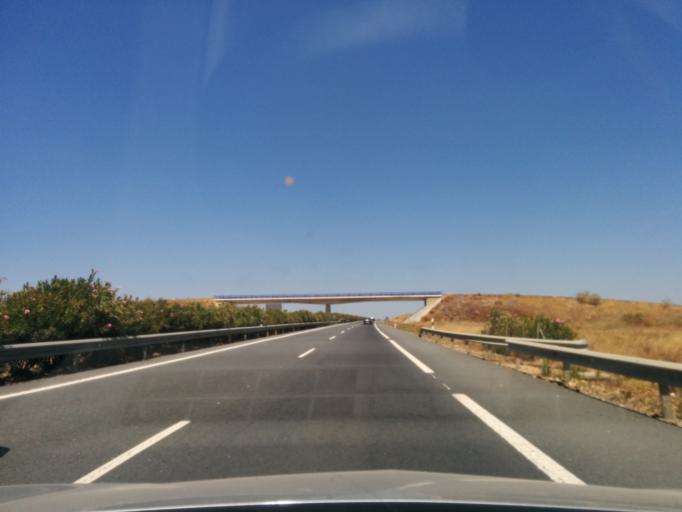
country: ES
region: Andalusia
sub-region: Provincia de Huelva
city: Gibraleon
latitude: 37.3329
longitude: -6.9165
